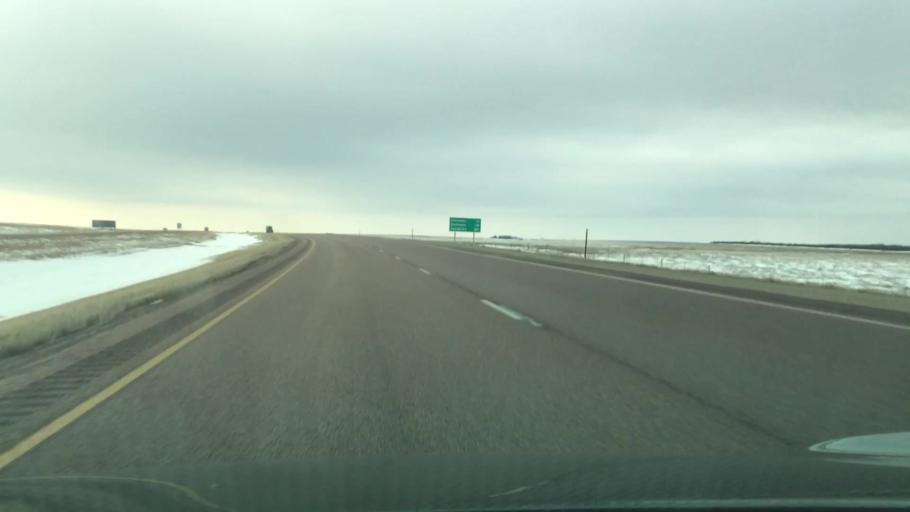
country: US
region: South Dakota
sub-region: Lyman County
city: Kennebec
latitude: 43.8687
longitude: -99.6209
